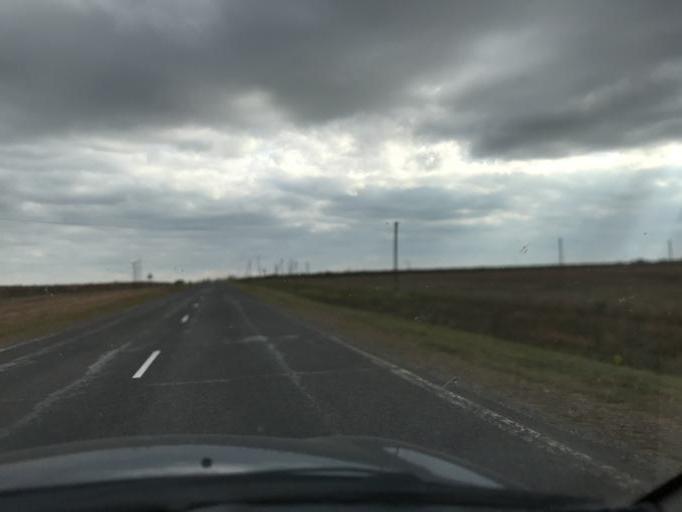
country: BY
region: Grodnenskaya
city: Lida
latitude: 53.8022
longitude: 25.1255
